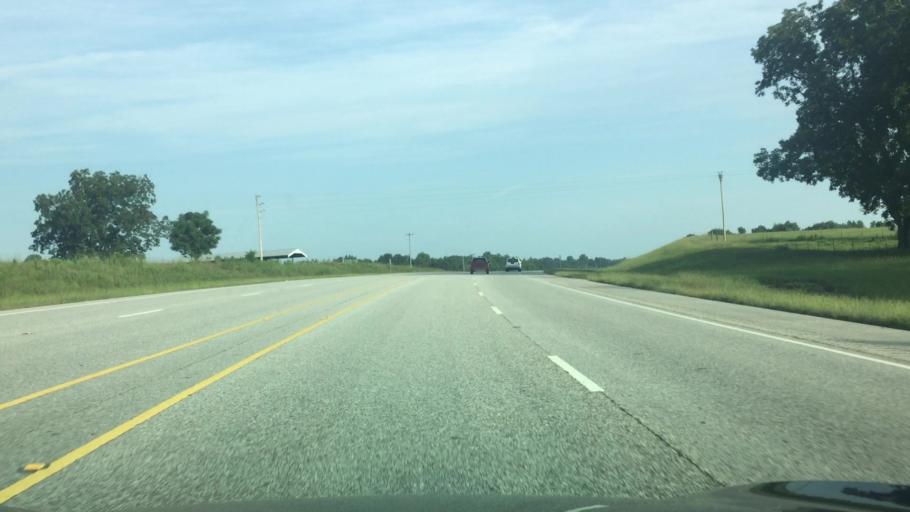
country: US
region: Alabama
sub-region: Butler County
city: Georgiana
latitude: 31.5195
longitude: -86.7124
